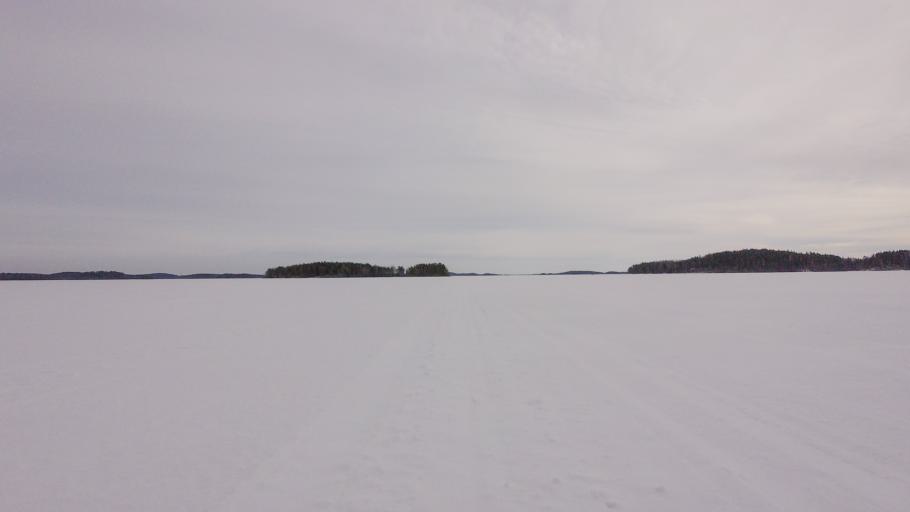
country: FI
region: Southern Savonia
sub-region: Savonlinna
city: Rantasalmi
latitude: 62.1140
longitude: 28.3657
